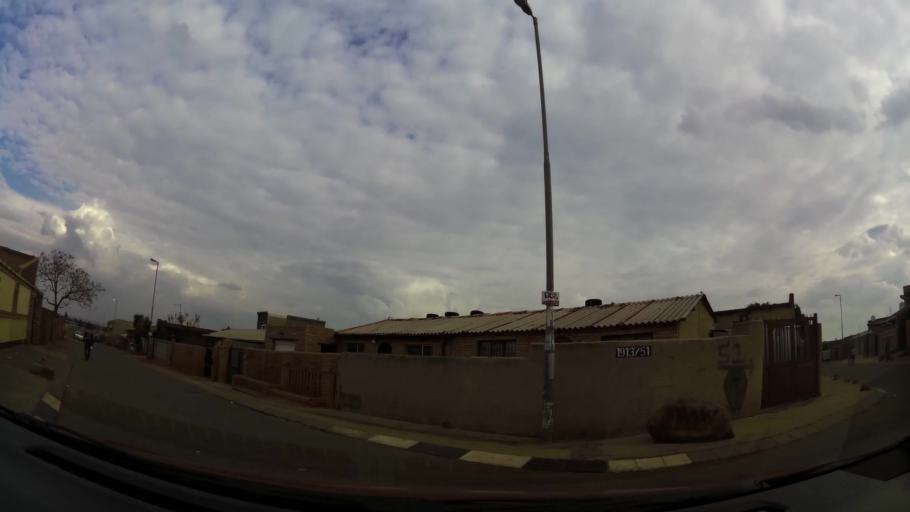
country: ZA
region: Gauteng
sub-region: City of Johannesburg Metropolitan Municipality
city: Soweto
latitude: -26.2435
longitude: 27.8358
